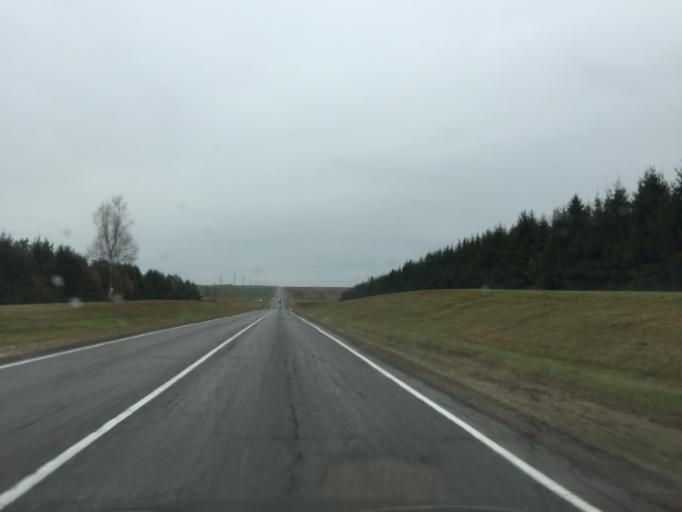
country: BY
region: Mogilev
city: Cherykaw
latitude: 53.6322
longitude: 31.2851
